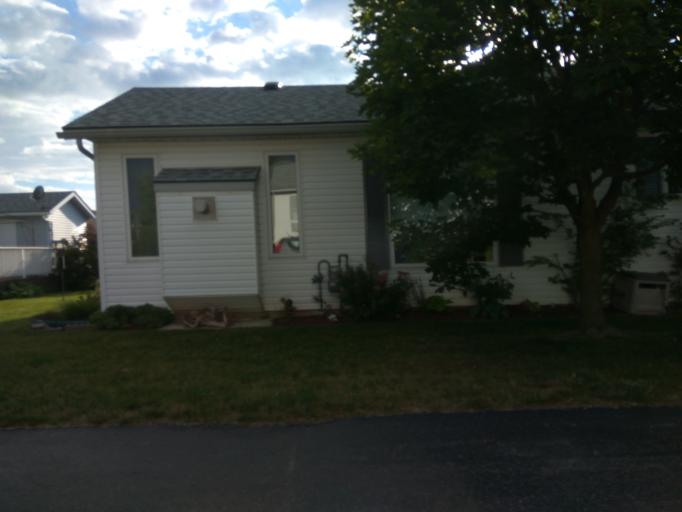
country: CA
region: Ontario
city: Kitchener
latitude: 43.3743
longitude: -80.6887
